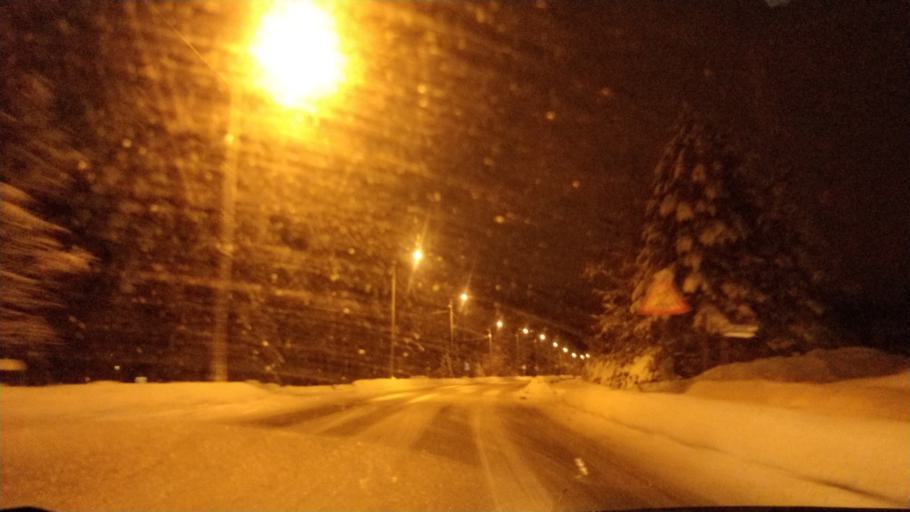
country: FI
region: Lapland
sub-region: Rovaniemi
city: Rovaniemi
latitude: 66.3742
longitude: 25.3830
